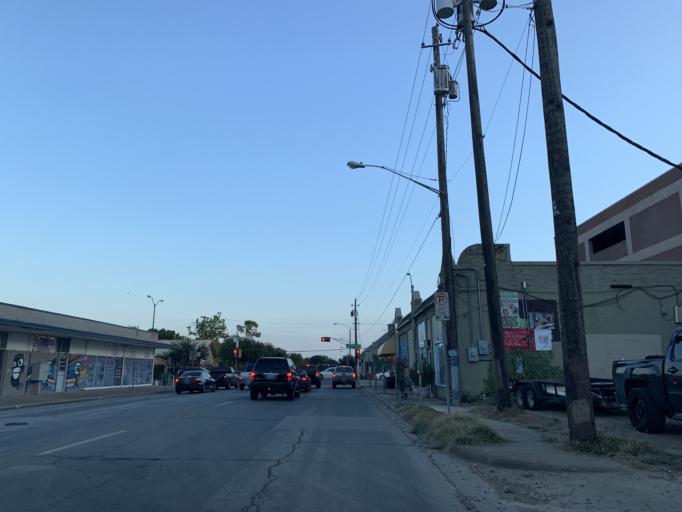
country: US
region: Texas
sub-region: Dallas County
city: Cockrell Hill
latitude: 32.7438
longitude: -96.8395
